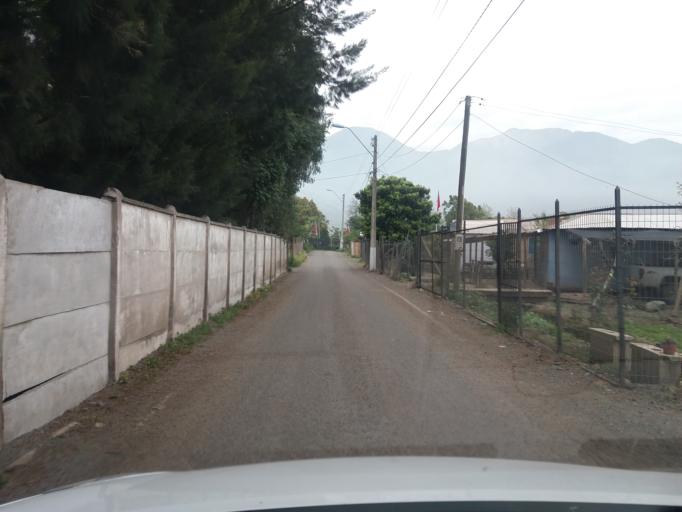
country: CL
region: Valparaiso
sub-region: Provincia de San Felipe
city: Llaillay
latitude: -32.8413
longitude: -71.0661
